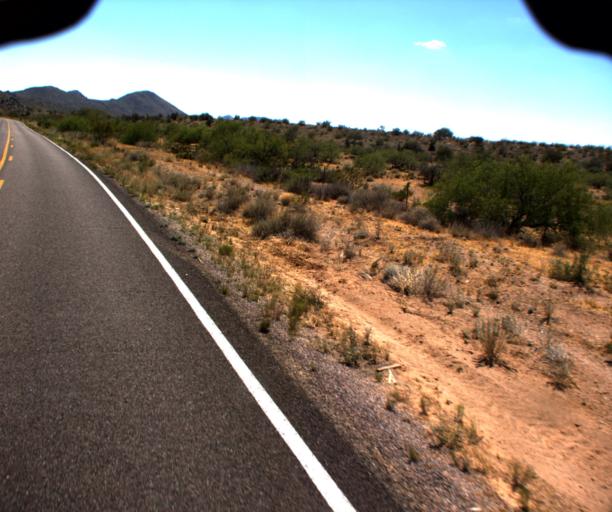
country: US
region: Arizona
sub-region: Yavapai County
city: Bagdad
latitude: 34.4961
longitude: -113.1764
